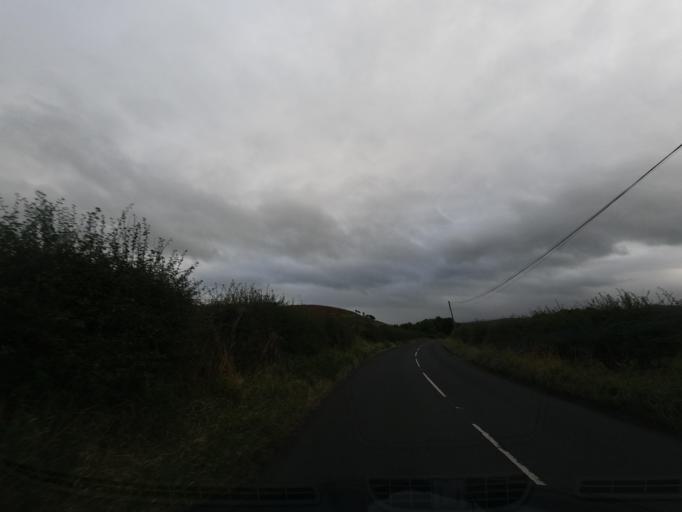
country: GB
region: England
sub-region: Northumberland
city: Doddington
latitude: 55.5912
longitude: -2.0020
